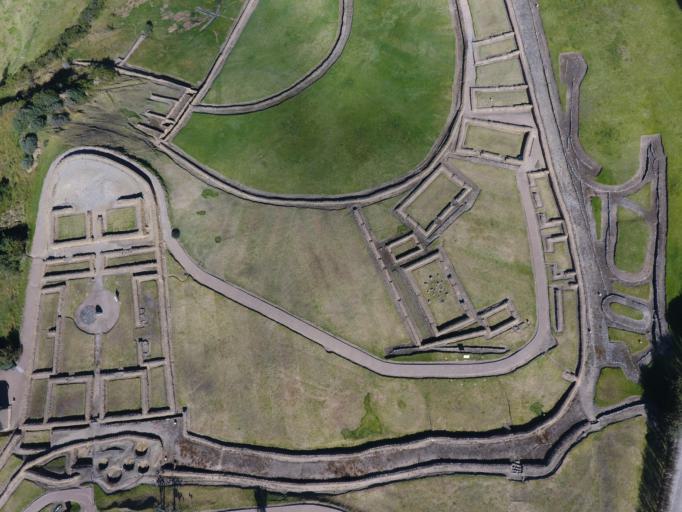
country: EC
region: Canar
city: Canar
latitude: -2.5407
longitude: -78.8734
